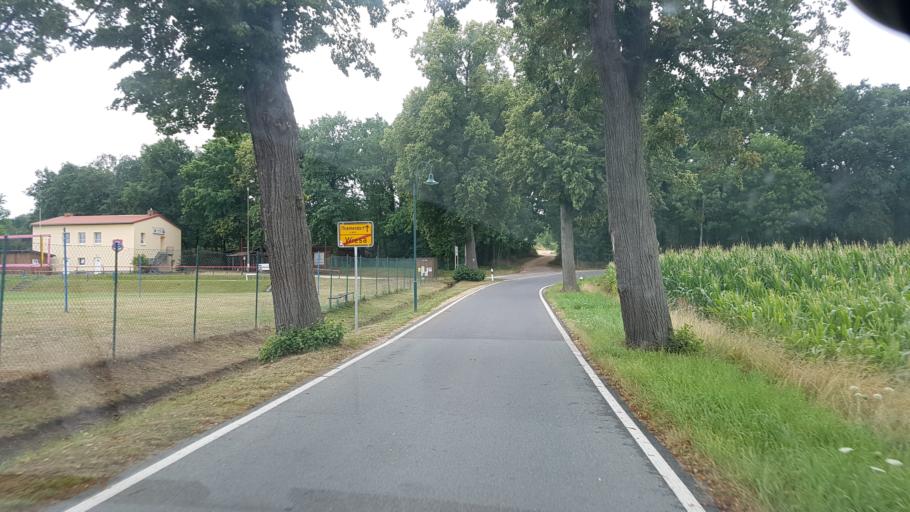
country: DE
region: Saxony
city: Kodersdorf
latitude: 51.2252
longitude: 14.8538
